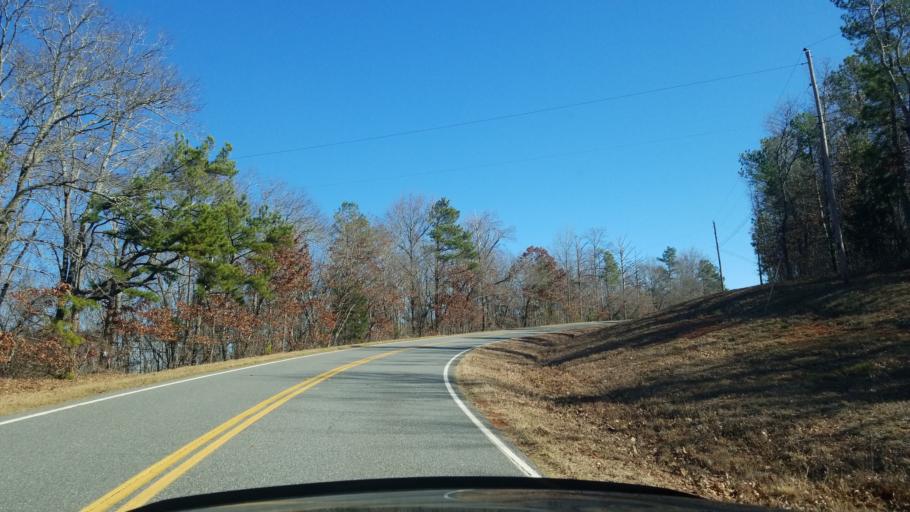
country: US
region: Georgia
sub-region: Meriwether County
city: Manchester
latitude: 32.8434
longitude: -84.6763
